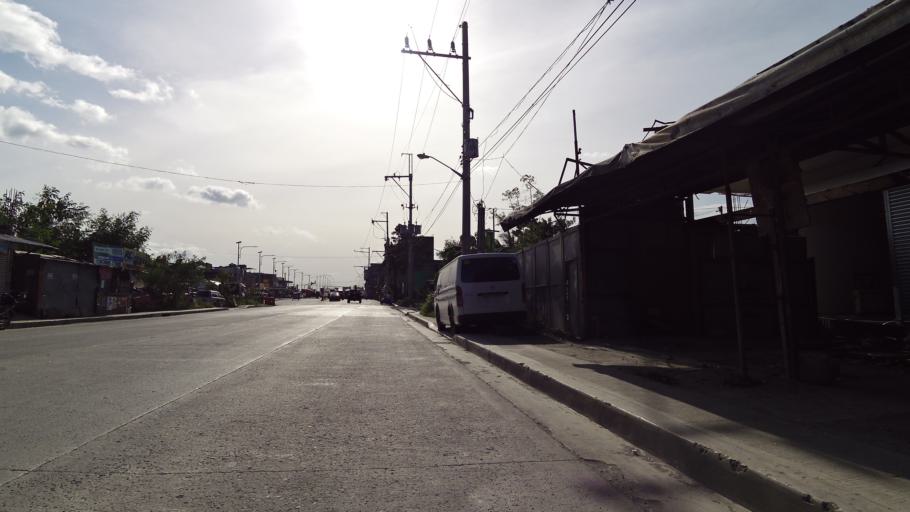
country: PH
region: Calabarzon
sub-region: Province of Rizal
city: Taytay
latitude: 14.5506
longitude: 121.1221
